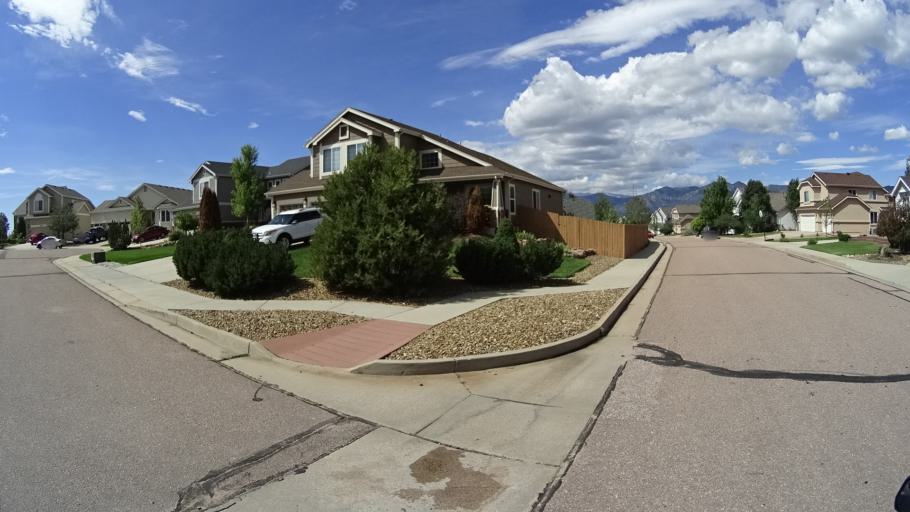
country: US
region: Colorado
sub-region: El Paso County
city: Gleneagle
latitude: 39.0308
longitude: -104.8194
